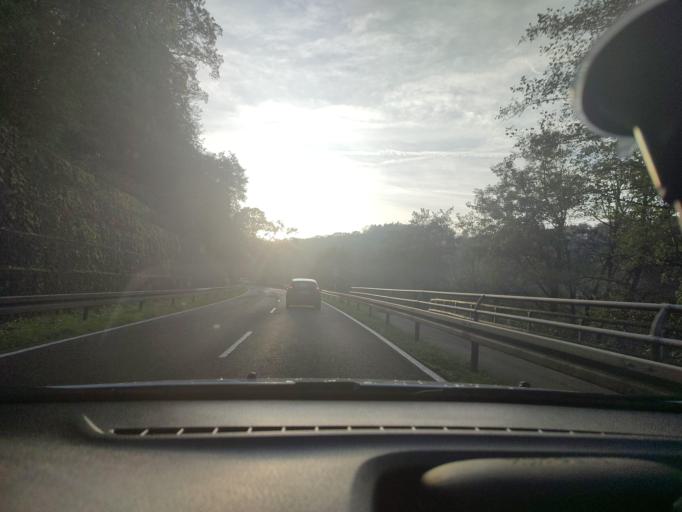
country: DE
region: Bavaria
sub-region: Regierungsbezirk Unterfranken
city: Marktheidenfeld
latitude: 49.8366
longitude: 9.5883
